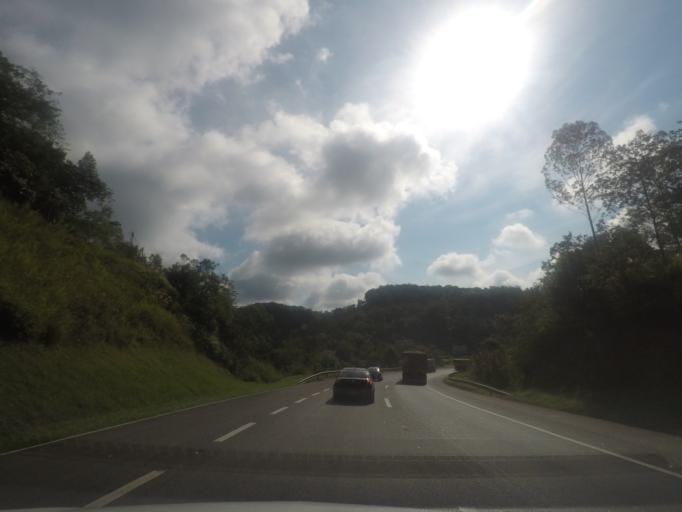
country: BR
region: Parana
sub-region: Antonina
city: Antonina
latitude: -25.5627
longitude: -48.8131
